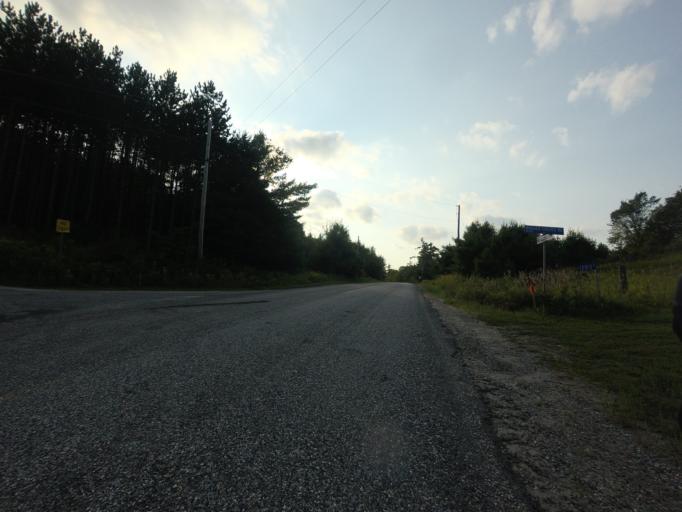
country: CA
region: Ontario
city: Perth
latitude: 44.9702
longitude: -76.7284
